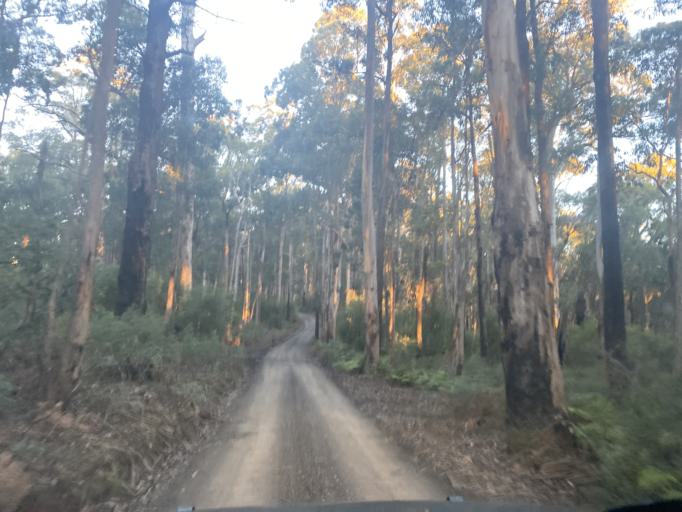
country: AU
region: Victoria
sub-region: Yarra Ranges
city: Healesville
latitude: -37.4351
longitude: 145.5323
